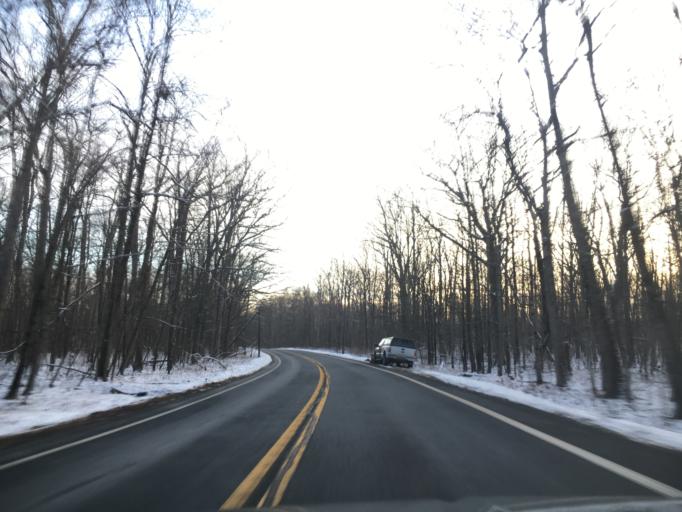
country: US
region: Pennsylvania
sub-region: Pike County
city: Hemlock Farms
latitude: 41.2234
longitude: -75.0805
